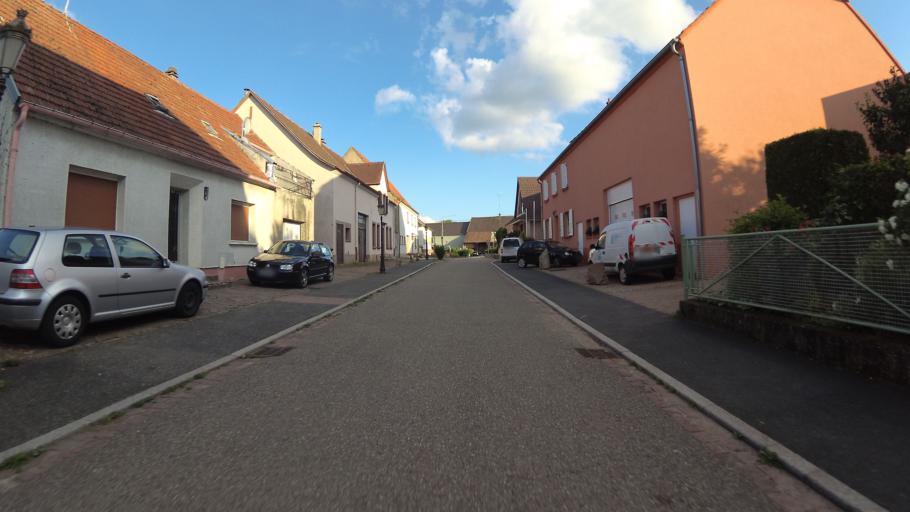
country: FR
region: Alsace
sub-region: Departement du Bas-Rhin
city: Oermingen
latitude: 49.0019
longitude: 7.1261
